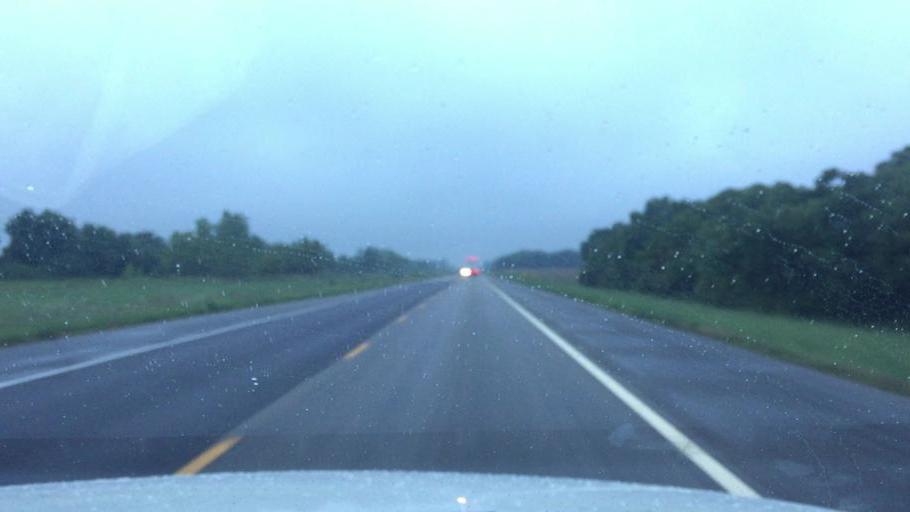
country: US
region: Kansas
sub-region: Montgomery County
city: Cherryvale
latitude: 37.4412
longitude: -95.4856
